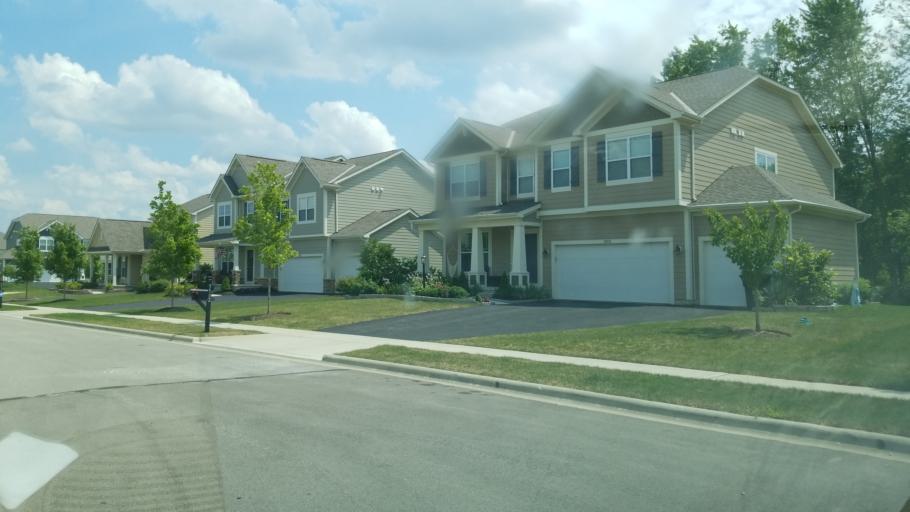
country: US
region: Ohio
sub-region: Delaware County
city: Lewis Center
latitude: 40.2113
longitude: -83.0178
